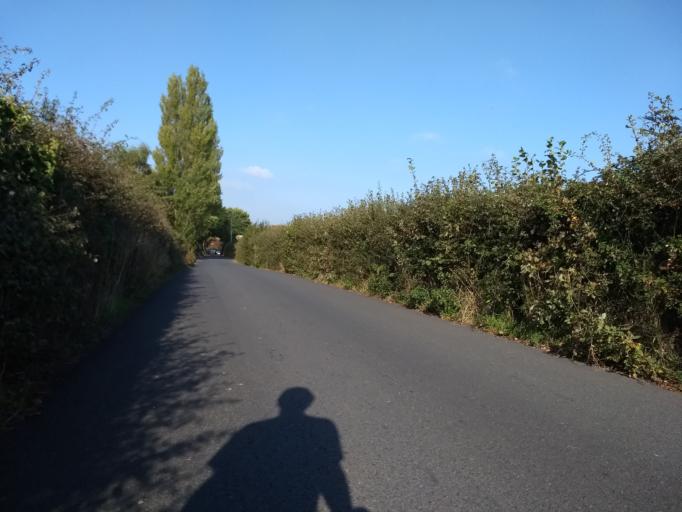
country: GB
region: England
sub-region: Isle of Wight
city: Newchurch
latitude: 50.7227
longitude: -1.2198
